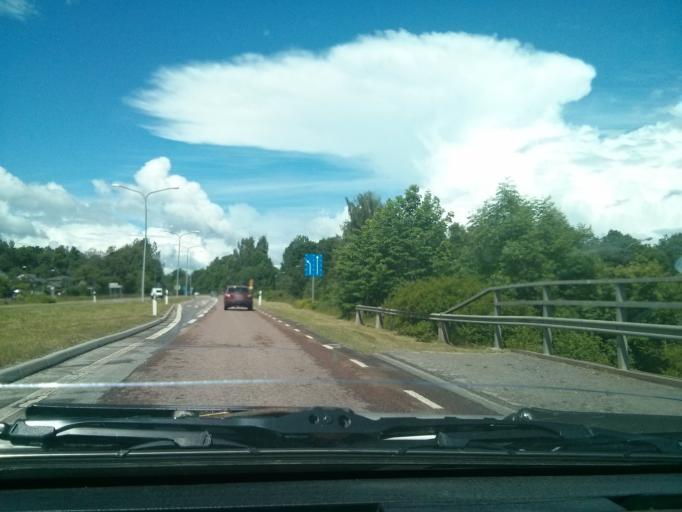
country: SE
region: Soedermanland
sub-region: Nykopings Kommun
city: Nykoping
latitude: 58.7720
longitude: 16.9844
